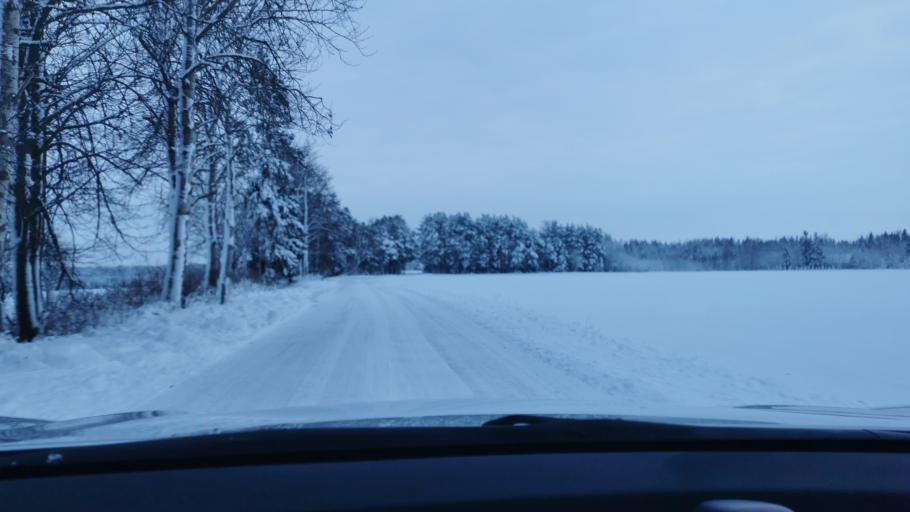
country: EE
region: Laeaene-Virumaa
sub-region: Haljala vald
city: Haljala
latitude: 59.5033
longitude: 26.2969
